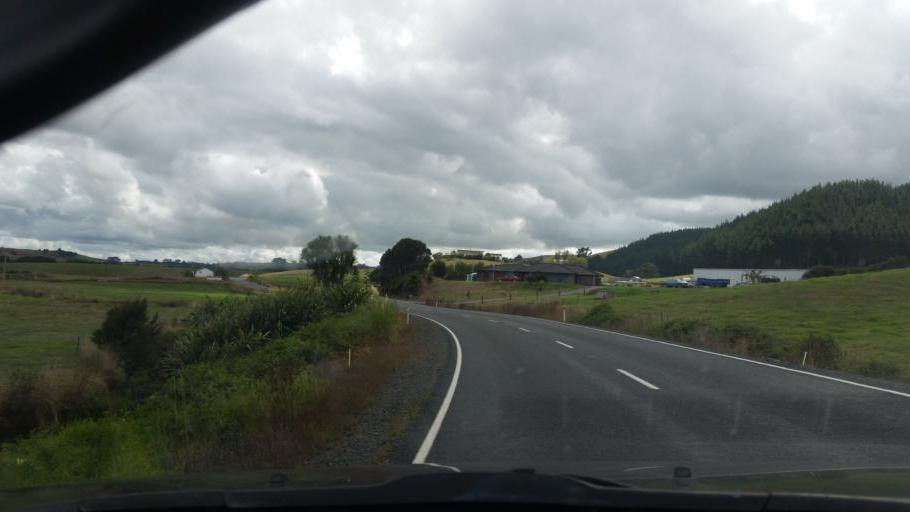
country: NZ
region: Northland
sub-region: Whangarei
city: Ruakaka
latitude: -35.9666
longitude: 174.2912
